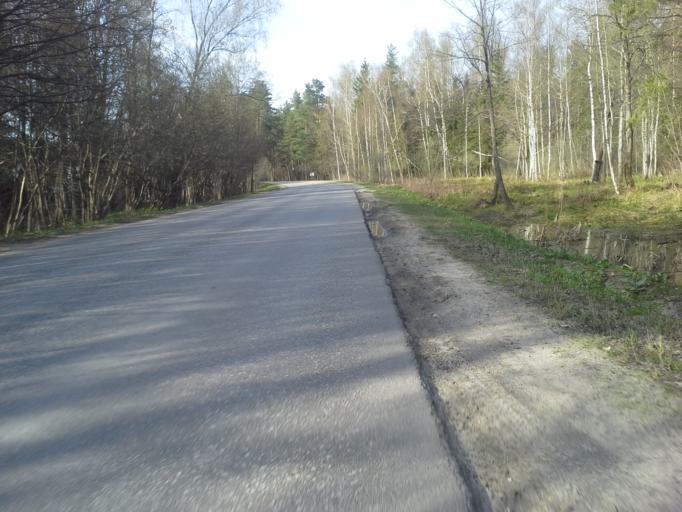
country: RU
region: Moskovskaya
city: Dubrovitsy
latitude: 55.4297
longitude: 37.3988
